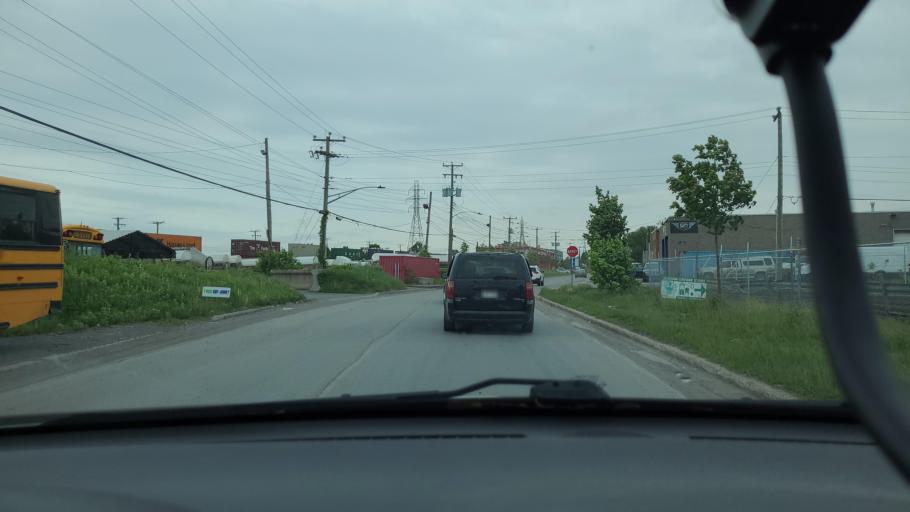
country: CA
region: Quebec
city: Montreal-Ouest
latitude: 45.4481
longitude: -73.6630
